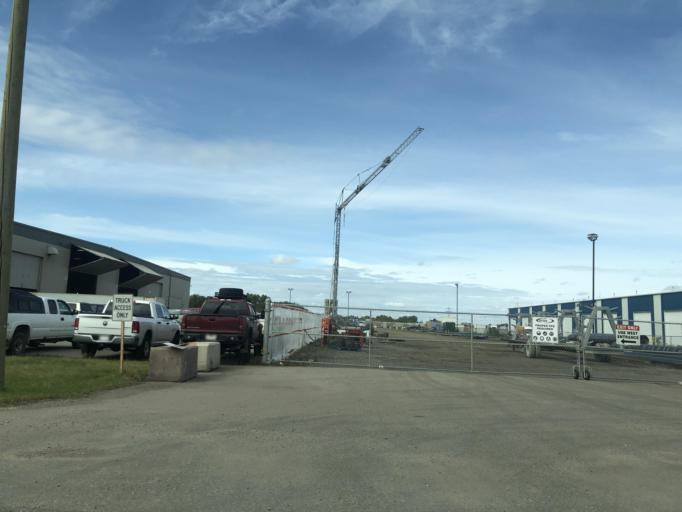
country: CA
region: Alberta
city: Chestermere
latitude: 50.9704
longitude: -113.9070
